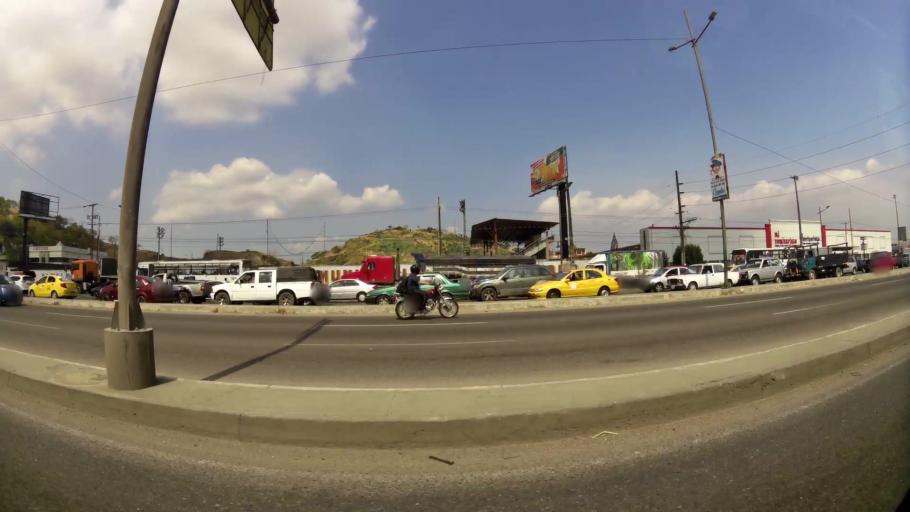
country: EC
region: Guayas
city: Eloy Alfaro
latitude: -2.1685
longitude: -79.8402
